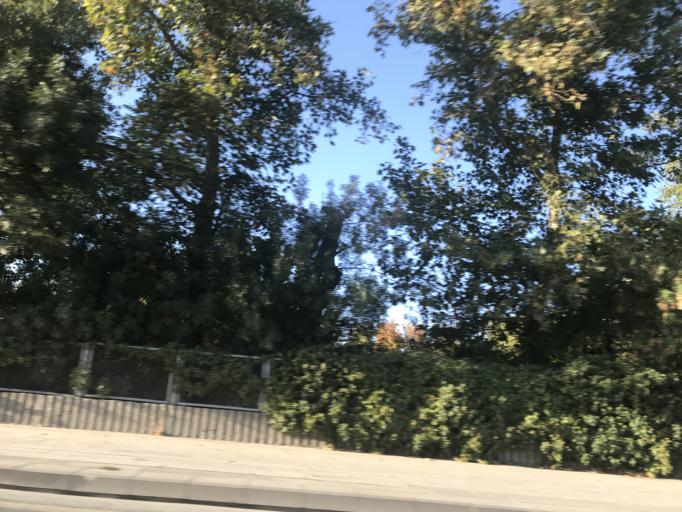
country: TR
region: Ankara
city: Ankara
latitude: 39.9555
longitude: 32.8279
